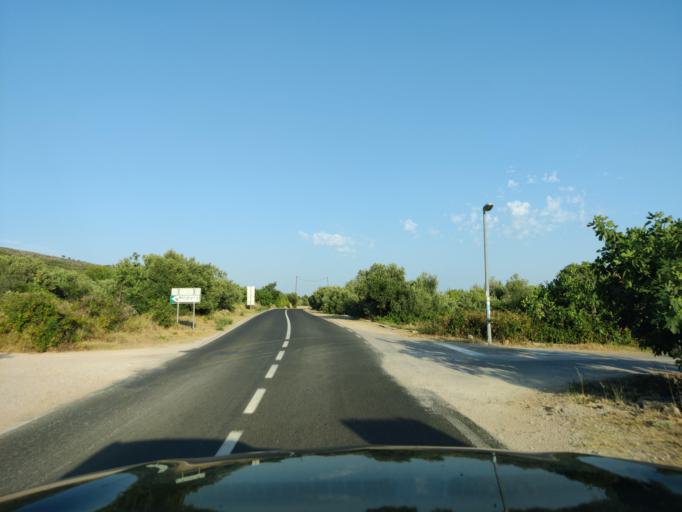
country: HR
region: Sibensko-Kniniska
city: Tribunj
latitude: 43.7684
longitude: 15.7301
